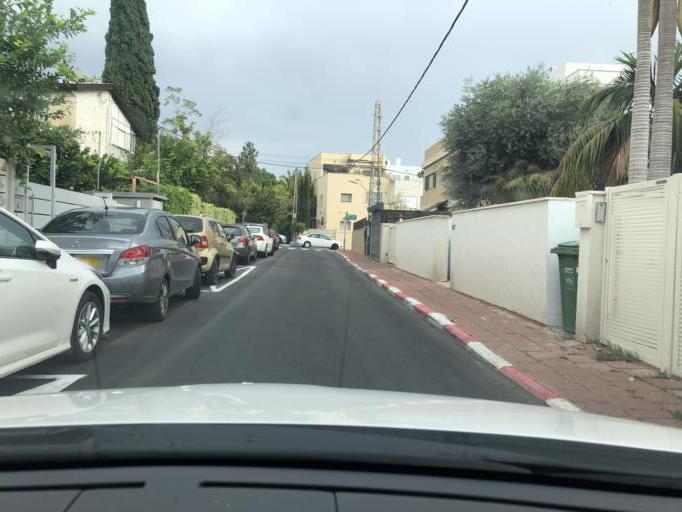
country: IL
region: Tel Aviv
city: Giv`atayim
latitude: 32.0554
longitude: 34.8198
